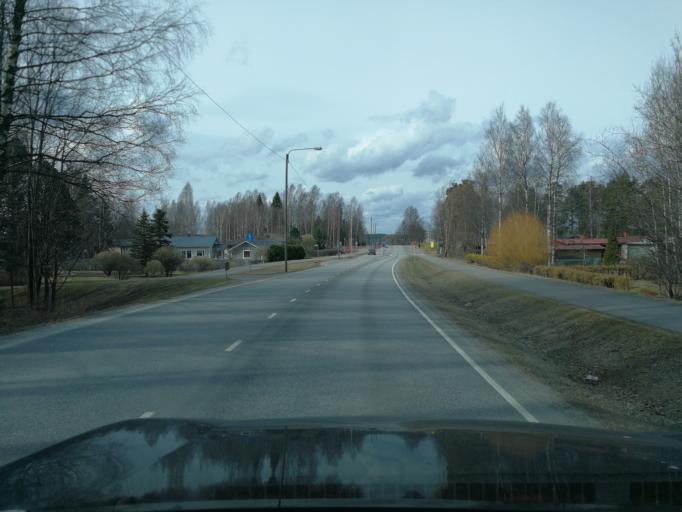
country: FI
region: Uusimaa
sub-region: Helsinki
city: Siuntio
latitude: 60.1330
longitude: 24.2307
